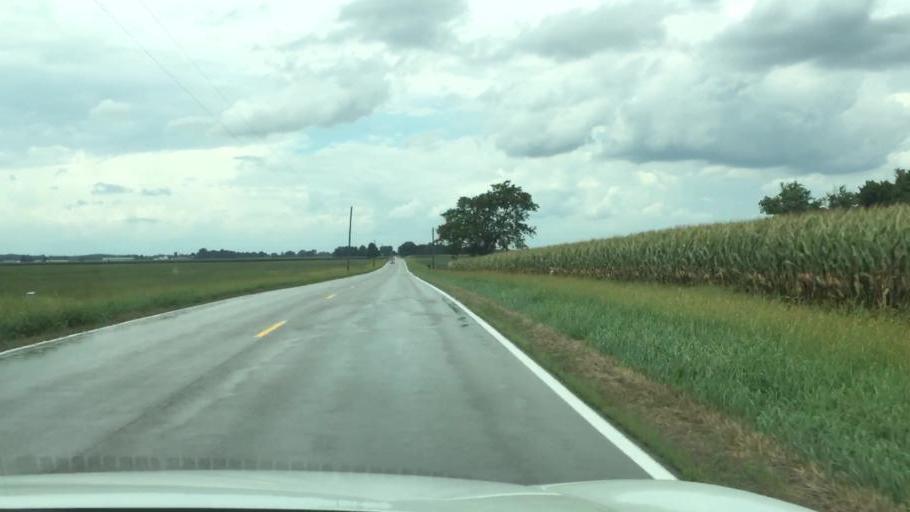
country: US
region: Ohio
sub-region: Clark County
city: Northridge
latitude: 40.0369
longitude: -83.7106
